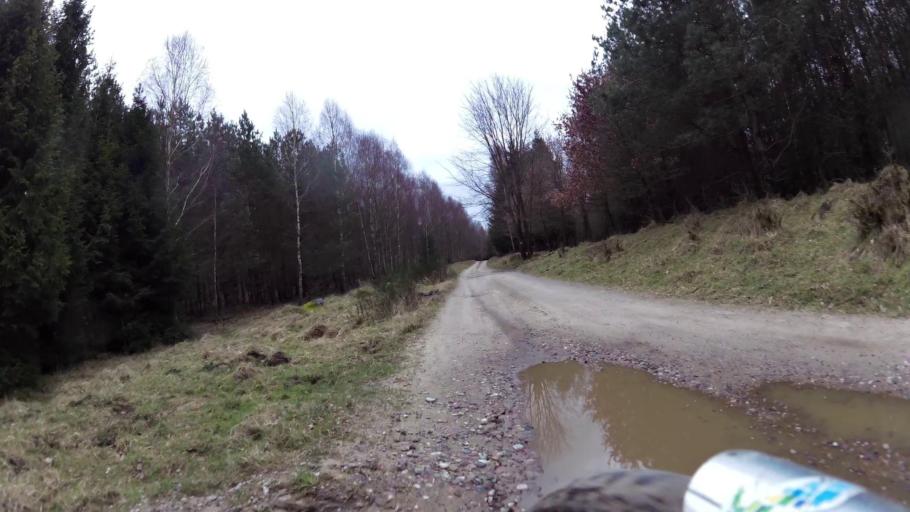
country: PL
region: Pomeranian Voivodeship
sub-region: Powiat bytowski
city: Trzebielino
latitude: 54.1145
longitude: 17.1288
